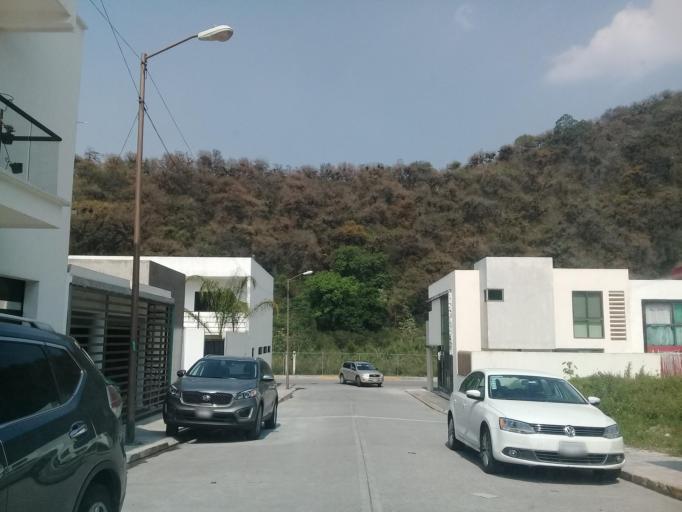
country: MX
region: Veracruz
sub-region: Mariano Escobedo
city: Palmira
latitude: 18.8787
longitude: -97.1030
